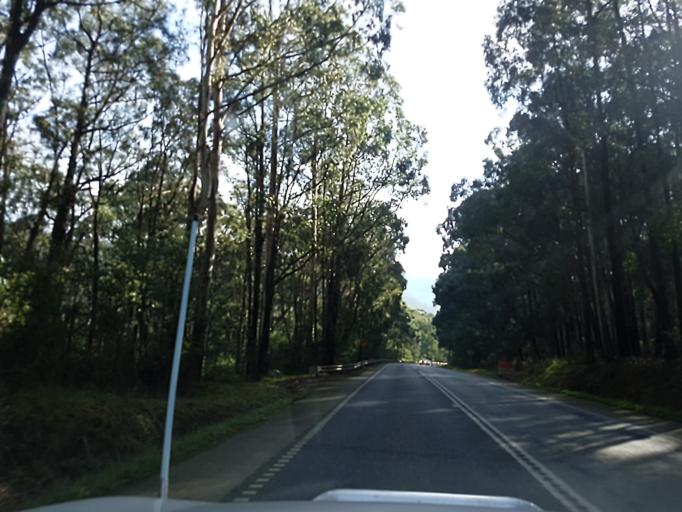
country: AU
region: Victoria
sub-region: Yarra Ranges
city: Yarra Glen
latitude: -37.5005
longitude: 145.4215
